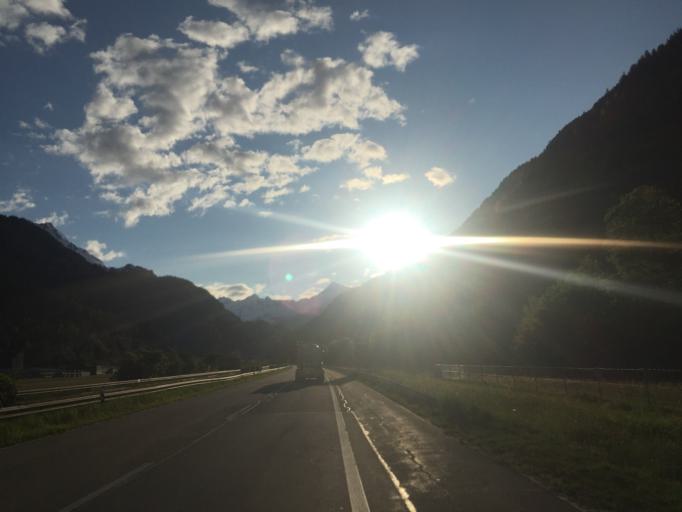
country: CH
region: Ticino
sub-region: Leventina District
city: Airolo
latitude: 46.5152
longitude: 8.6892
